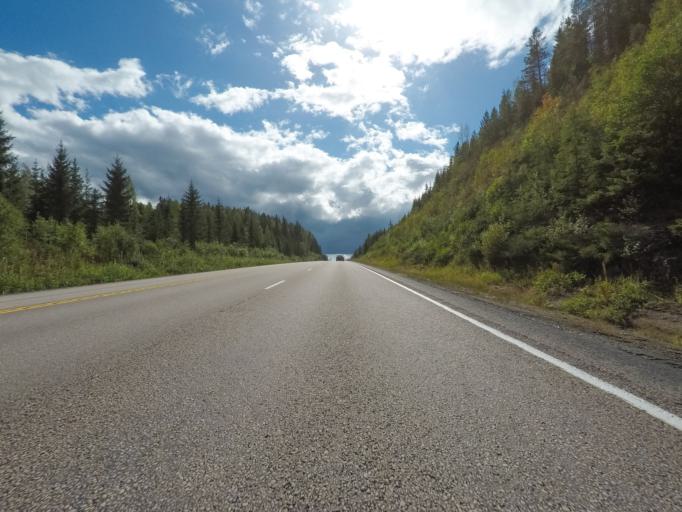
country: FI
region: Central Finland
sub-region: Jyvaeskylae
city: Toivakka
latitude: 62.0496
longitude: 26.0518
